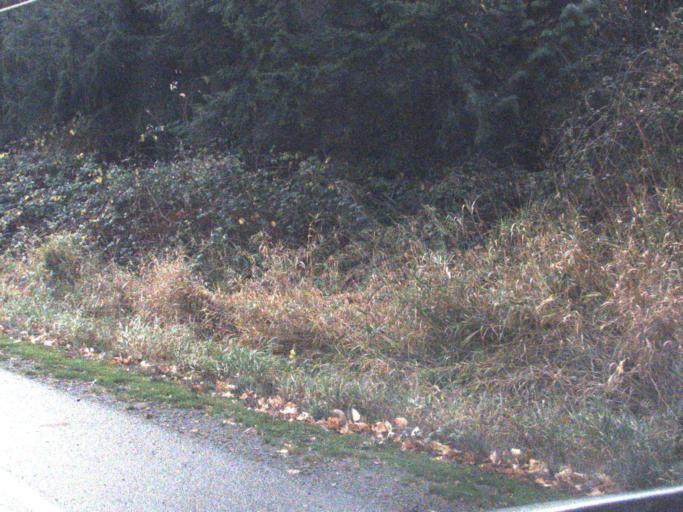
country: US
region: Washington
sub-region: Snohomish County
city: Cathcart
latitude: 47.8620
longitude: -122.1099
